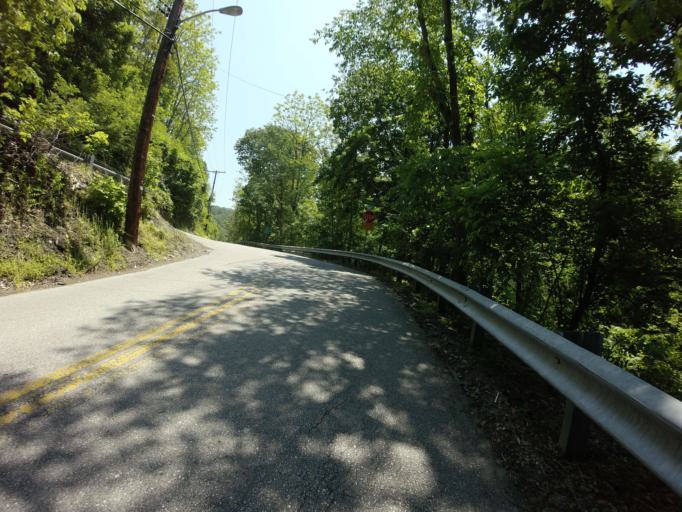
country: US
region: Maryland
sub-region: Howard County
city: Ilchester
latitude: 39.2529
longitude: -76.7683
